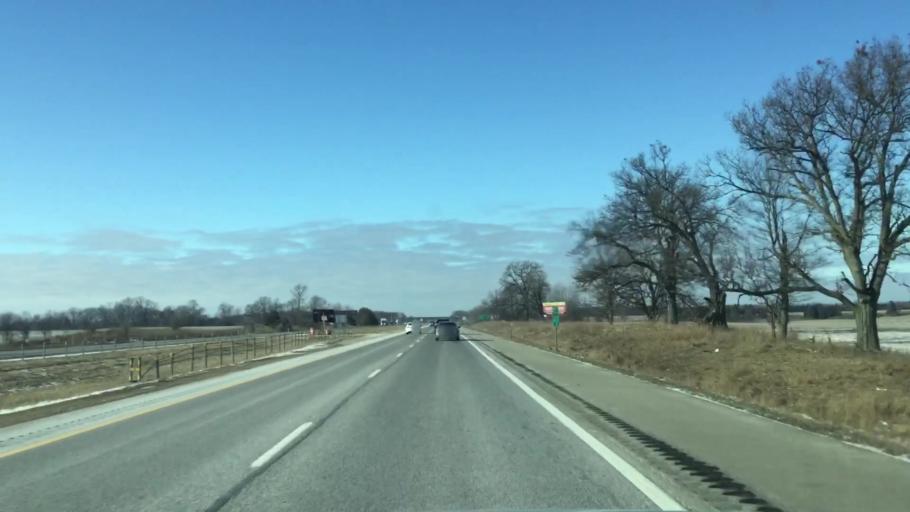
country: US
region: Michigan
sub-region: Calhoun County
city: Marshall
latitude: 42.2983
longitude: -85.0158
